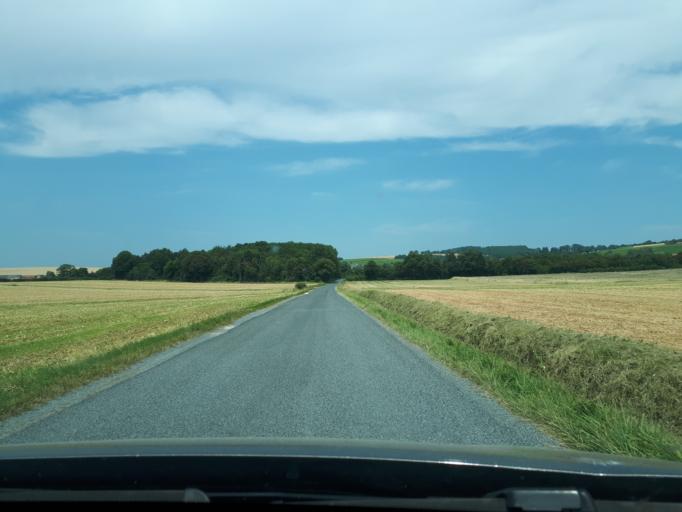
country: FR
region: Centre
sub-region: Departement du Cher
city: Sancerre
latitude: 47.2953
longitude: 2.7513
